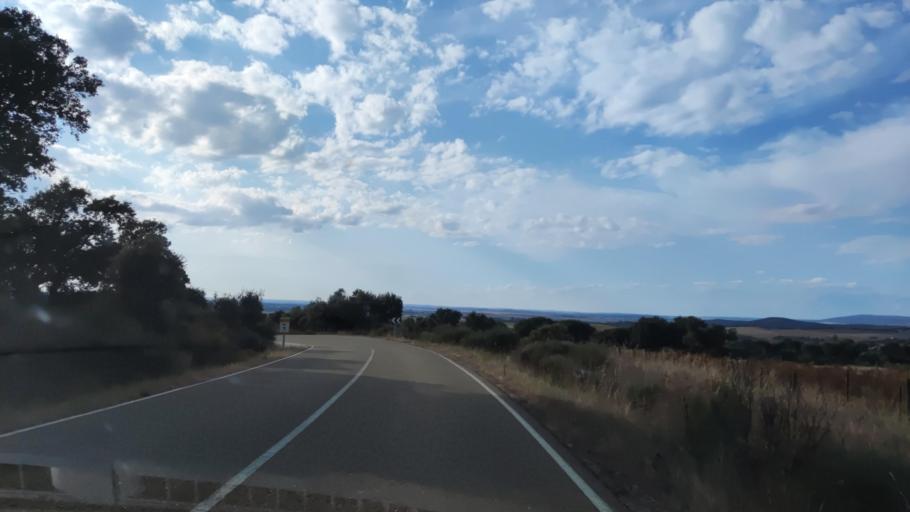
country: ES
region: Castille and Leon
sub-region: Provincia de Salamanca
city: Pastores
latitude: 40.5240
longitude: -6.5196
